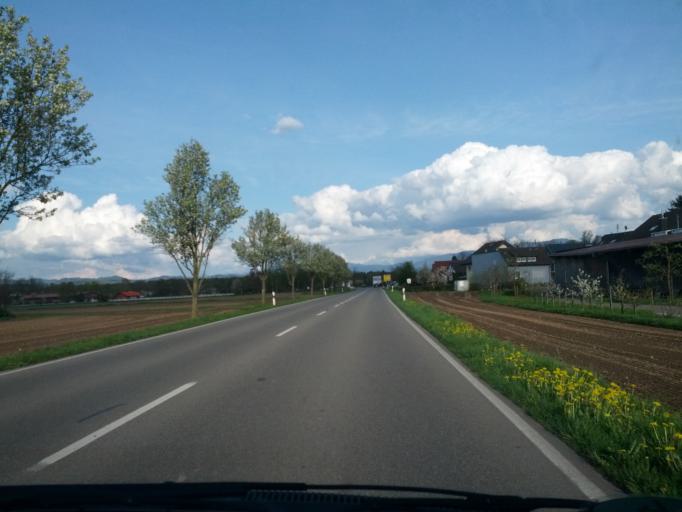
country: DE
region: Baden-Wuerttemberg
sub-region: Freiburg Region
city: Eichstetten
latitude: 48.1079
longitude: 7.7738
